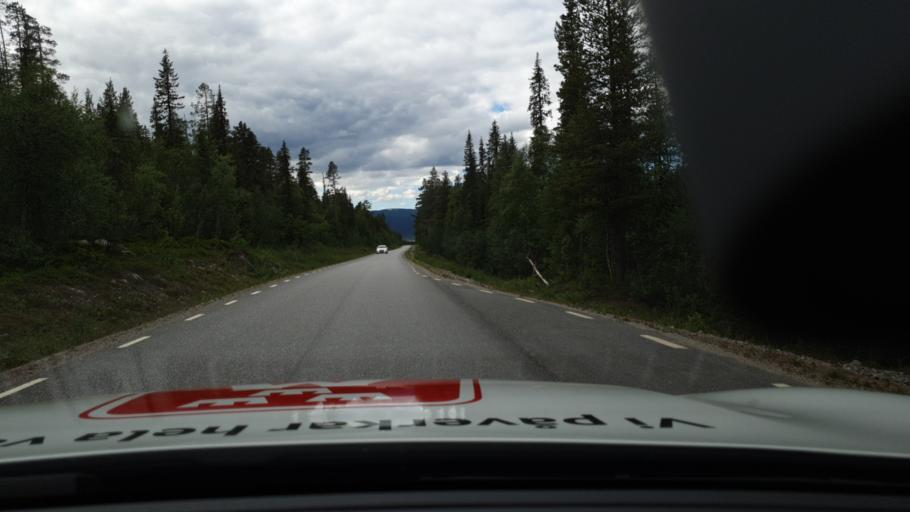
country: SE
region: Norrbotten
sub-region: Arjeplogs Kommun
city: Arjeplog
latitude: 66.8947
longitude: 17.9483
